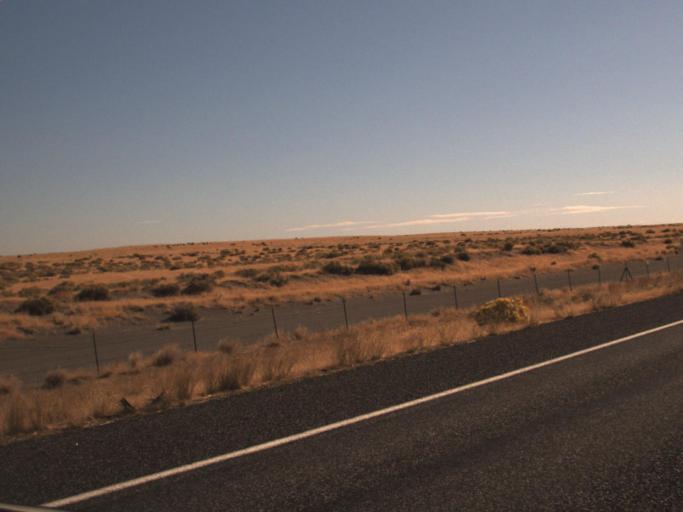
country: US
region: Washington
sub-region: Benton County
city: Benton City
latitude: 46.4405
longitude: -119.4898
